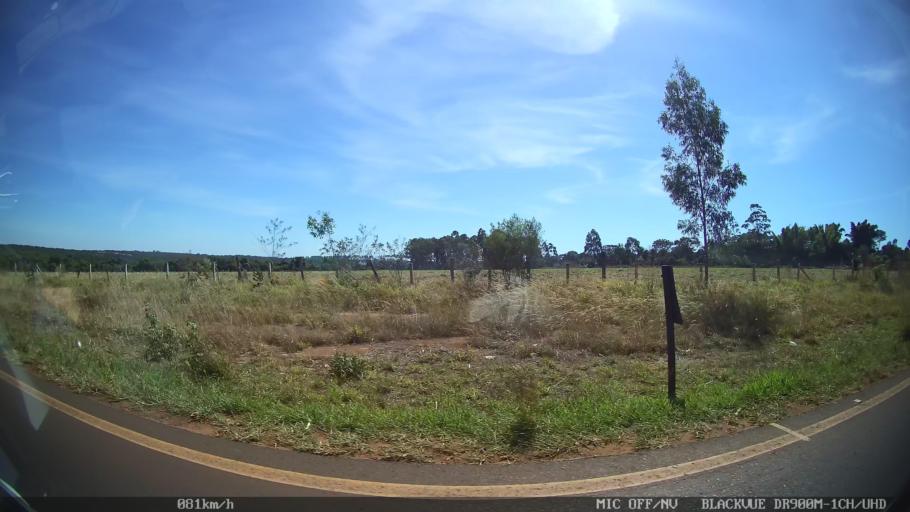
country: BR
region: Sao Paulo
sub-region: Franca
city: Franca
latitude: -20.5571
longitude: -47.4986
